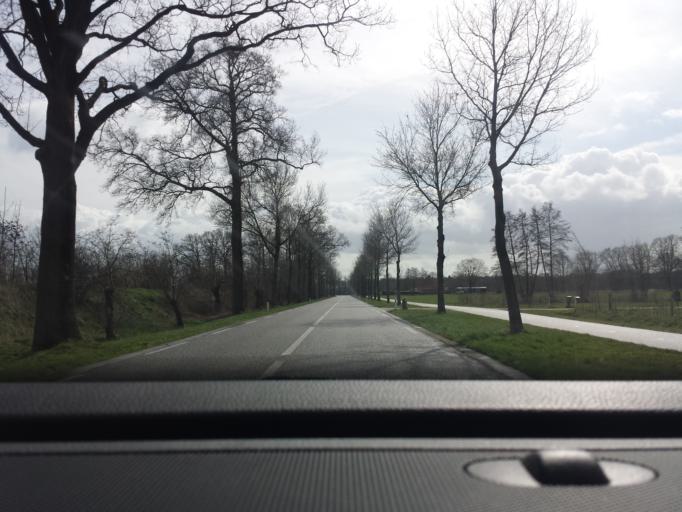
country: NL
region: Gelderland
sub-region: Oude IJsselstreek
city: Varsseveld
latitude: 51.9745
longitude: 6.4421
